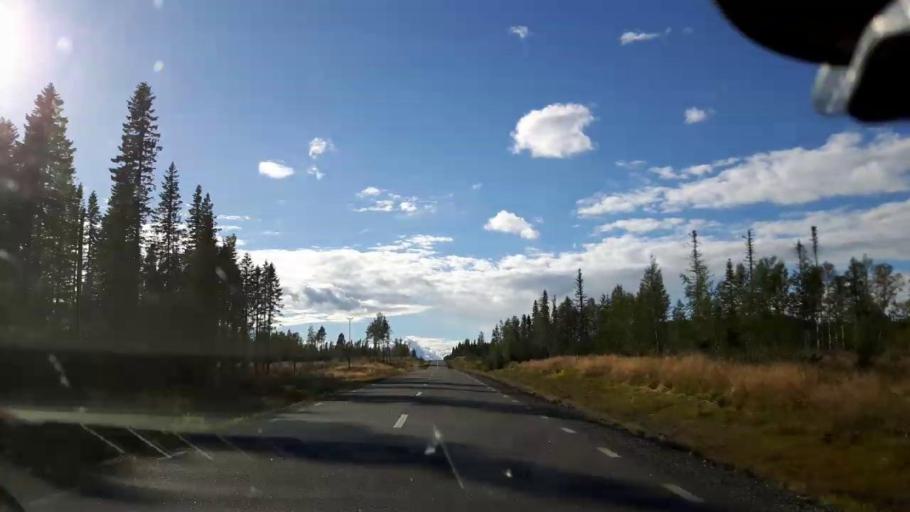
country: SE
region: Jaemtland
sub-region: Stroemsunds Kommun
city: Stroemsund
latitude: 63.5418
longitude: 15.9477
